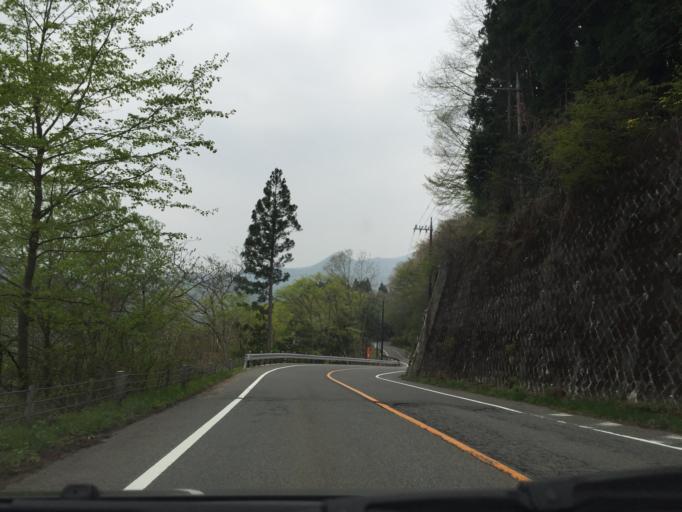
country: JP
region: Tochigi
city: Nikko
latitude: 36.9372
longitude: 139.6955
